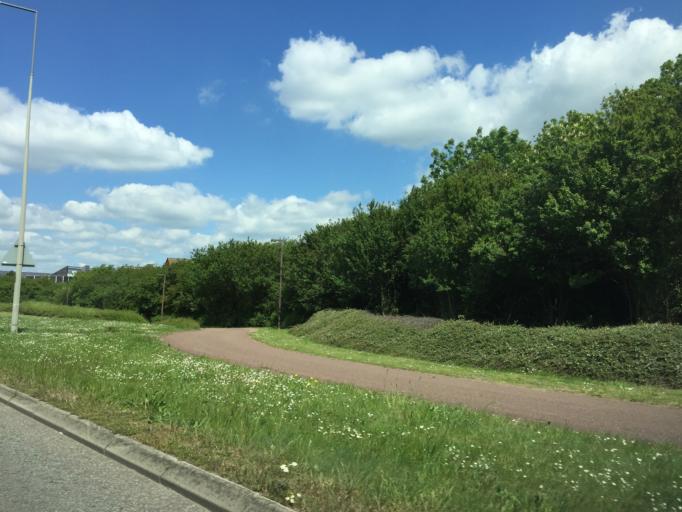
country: GB
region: England
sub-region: Milton Keynes
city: Broughton
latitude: 52.0362
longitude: -0.7089
